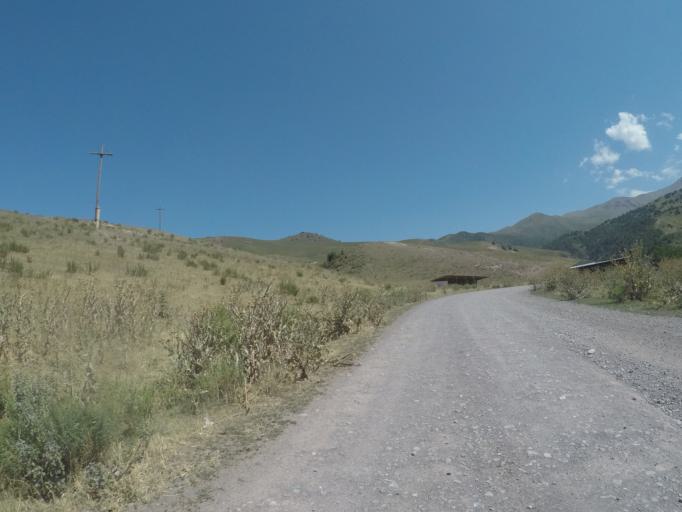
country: KG
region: Chuy
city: Bishkek
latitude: 42.6488
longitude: 74.5117
